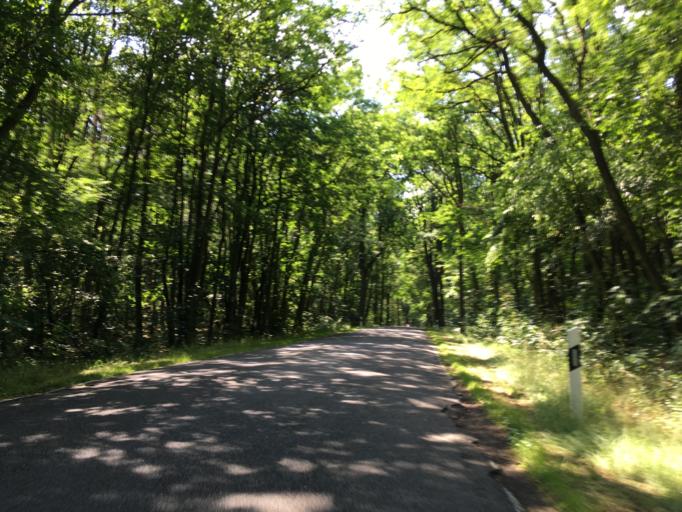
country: DE
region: Brandenburg
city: Hohenfinow
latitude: 52.7901
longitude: 13.9010
